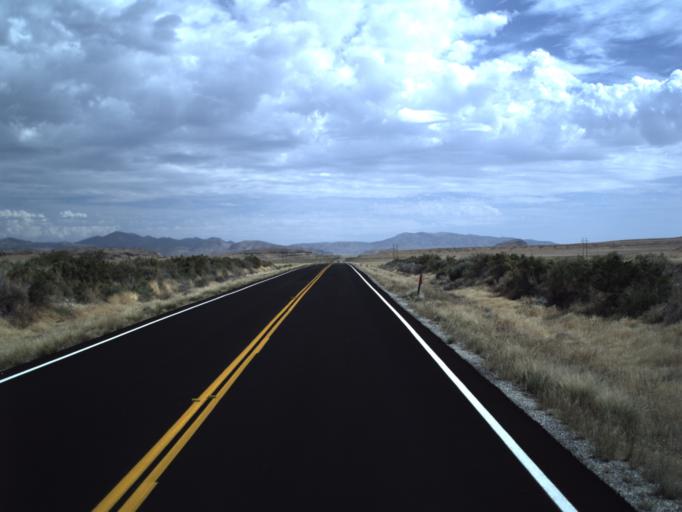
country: US
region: Utah
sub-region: Tooele County
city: Wendover
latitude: 41.4091
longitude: -113.9322
